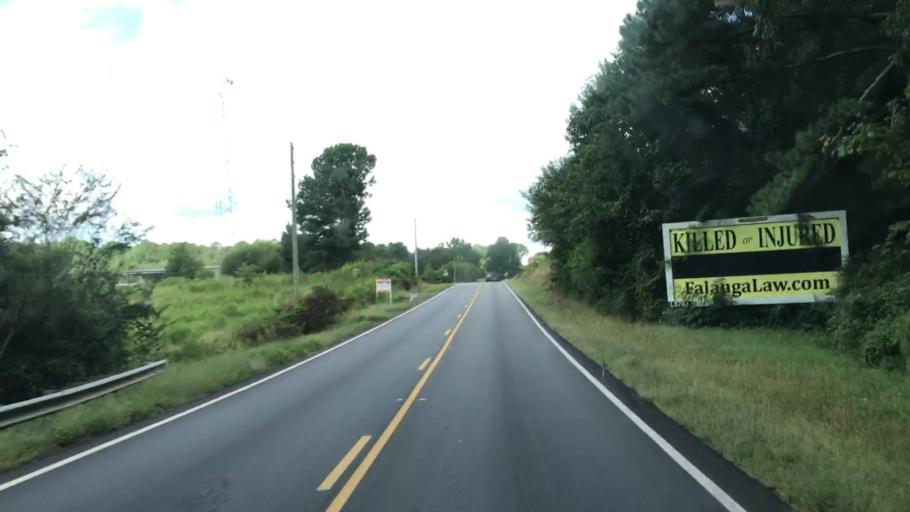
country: US
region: Georgia
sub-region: Greene County
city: Greensboro
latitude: 33.5695
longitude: -83.1637
